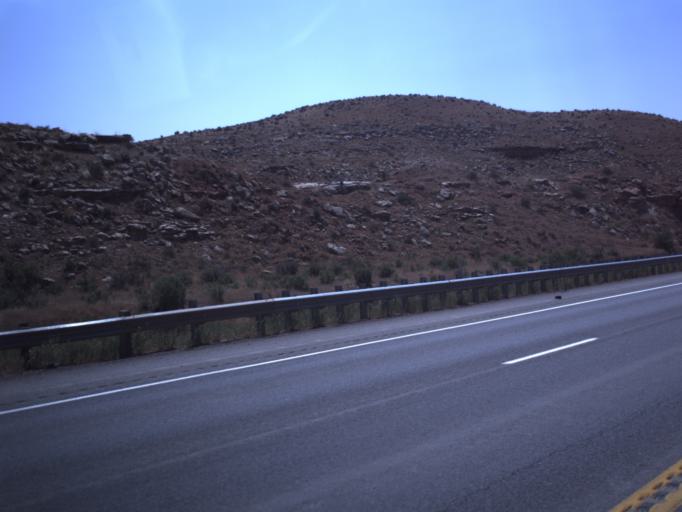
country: US
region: Utah
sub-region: Uintah County
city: Maeser
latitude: 40.3432
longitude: -109.6277
